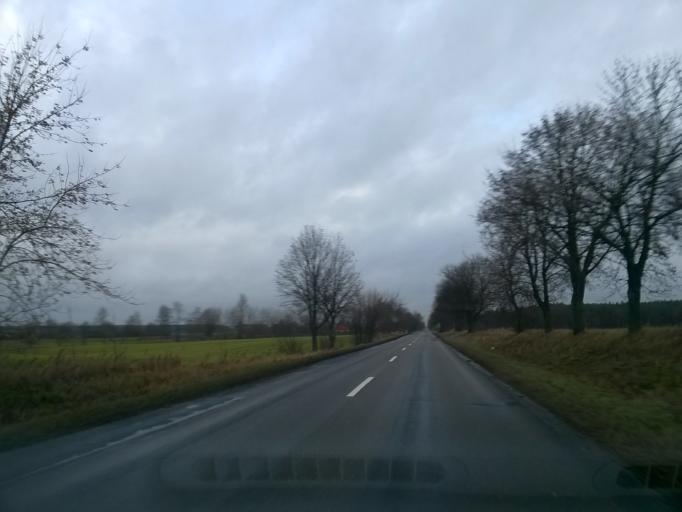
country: PL
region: Greater Poland Voivodeship
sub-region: Powiat wagrowiecki
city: Golancz
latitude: 52.9103
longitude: 17.3639
